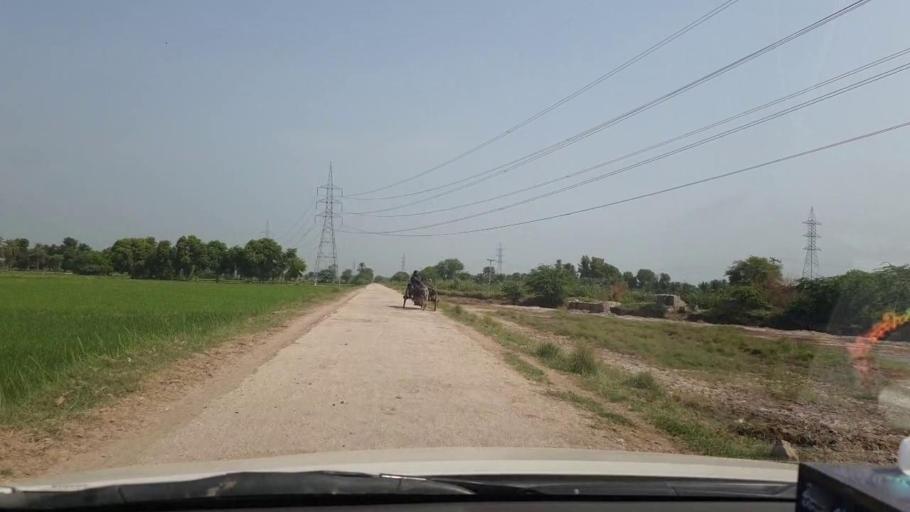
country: PK
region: Sindh
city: Shikarpur
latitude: 27.9768
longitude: 68.6645
